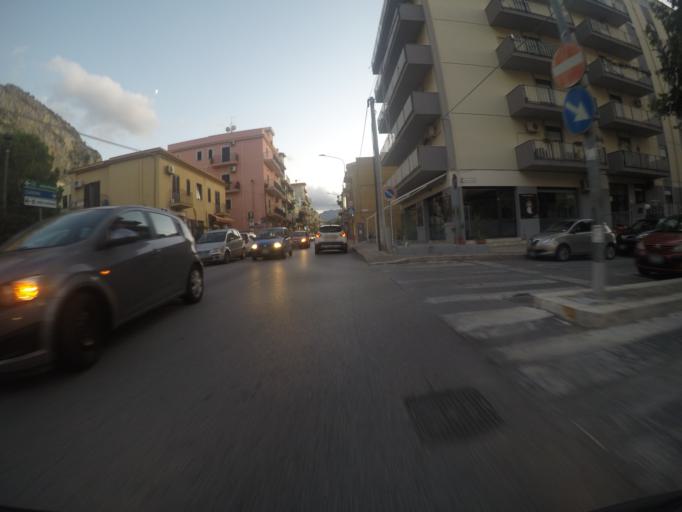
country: IT
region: Sicily
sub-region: Palermo
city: Capaci
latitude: 38.1760
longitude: 13.2424
